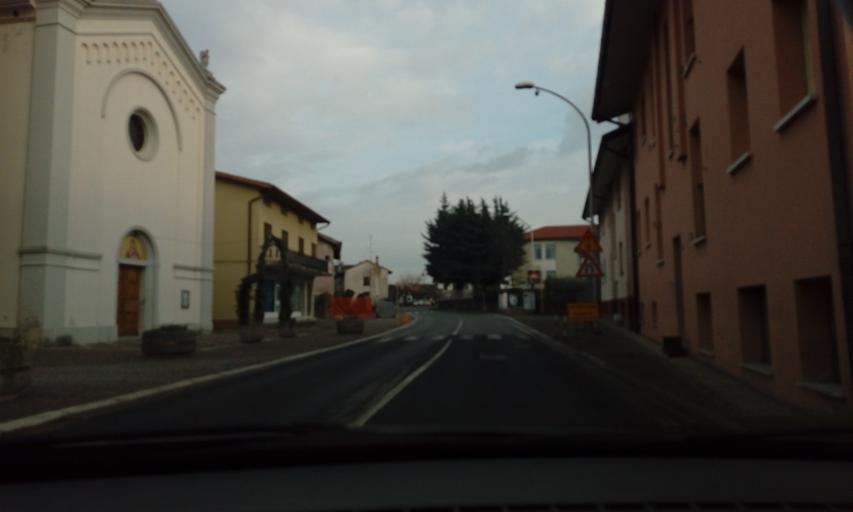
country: IT
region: Friuli Venezia Giulia
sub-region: Provincia di Udine
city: Corno di Rosazzo
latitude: 45.9856
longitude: 13.4267
